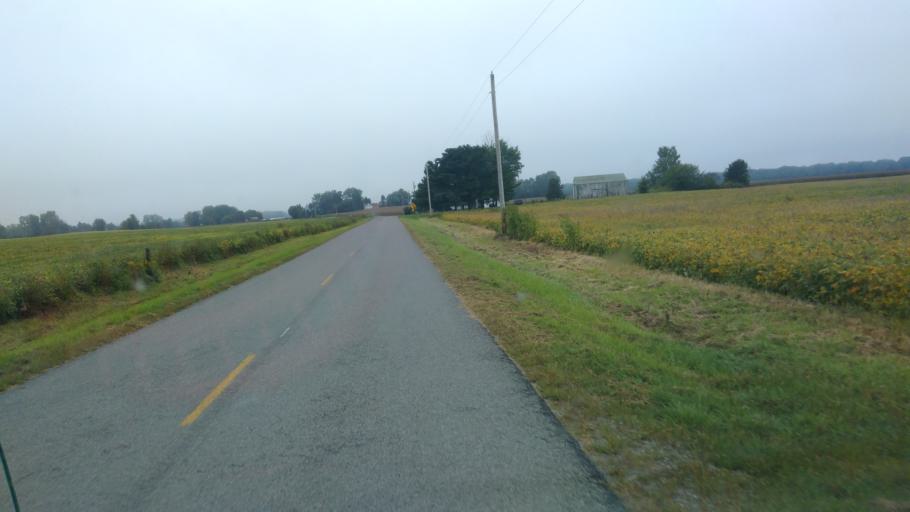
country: US
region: Ohio
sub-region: Logan County
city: Northwood
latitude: 40.4785
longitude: -83.5875
